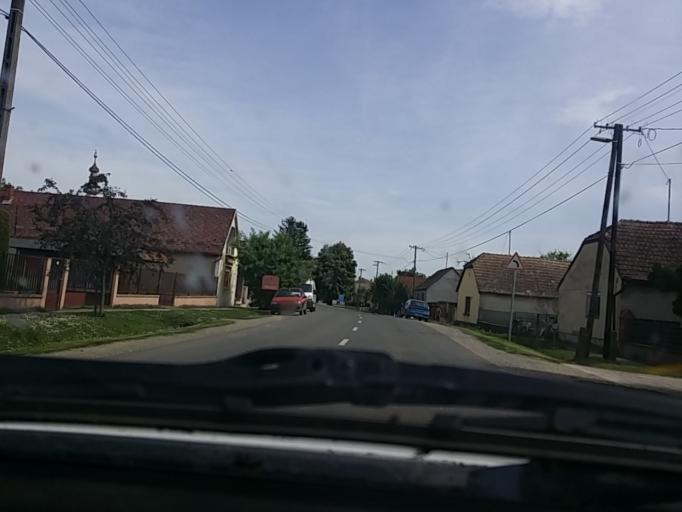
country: HR
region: Osjecko-Baranjska
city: Viljevo
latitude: 45.8252
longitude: 18.0994
